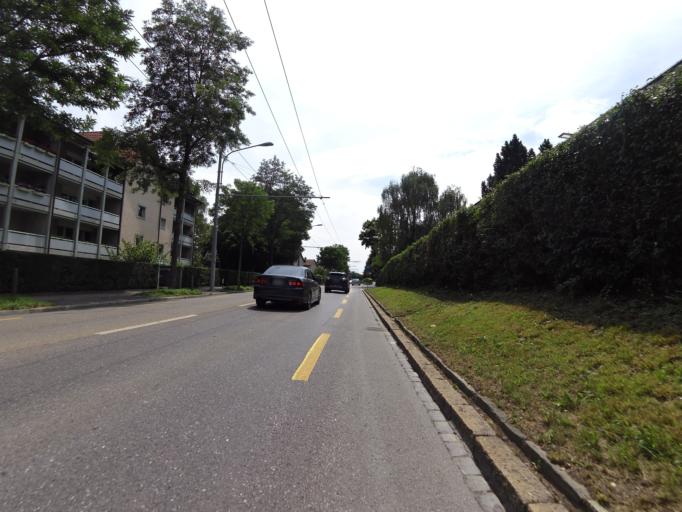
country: CH
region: Zurich
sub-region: Bezirk Zuerich
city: Zuerich (Kreis 3)
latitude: 47.3584
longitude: 8.5084
